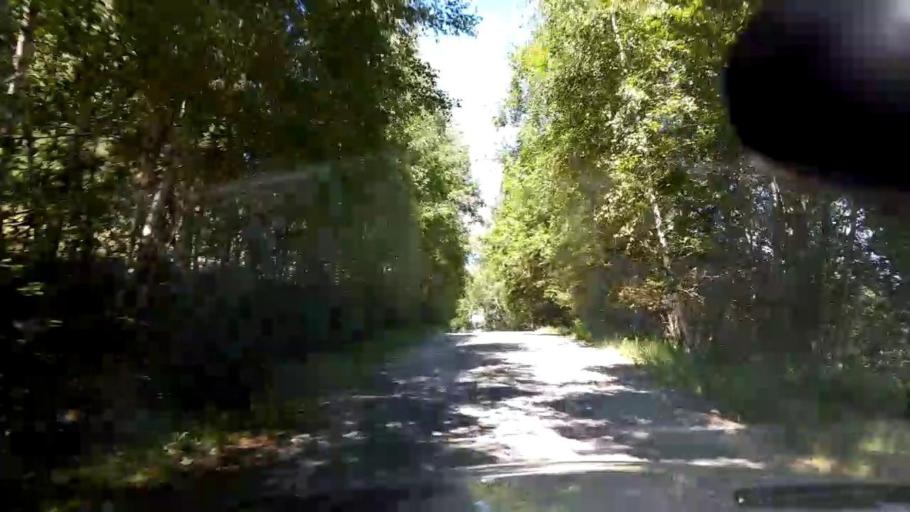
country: SE
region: Uppsala
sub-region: Habo Kommun
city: Balsta
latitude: 59.6179
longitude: 17.6130
